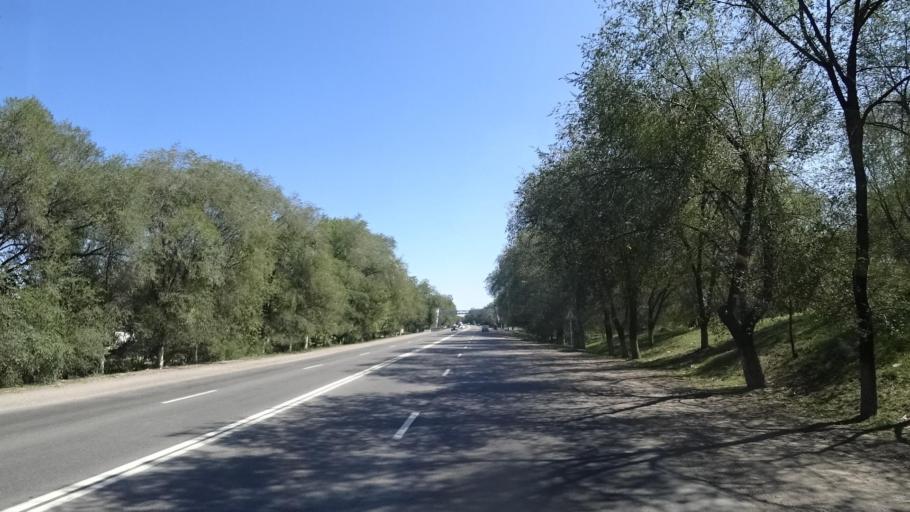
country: KZ
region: Almaty Oblysy
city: Talghar
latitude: 43.4026
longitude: 77.1907
